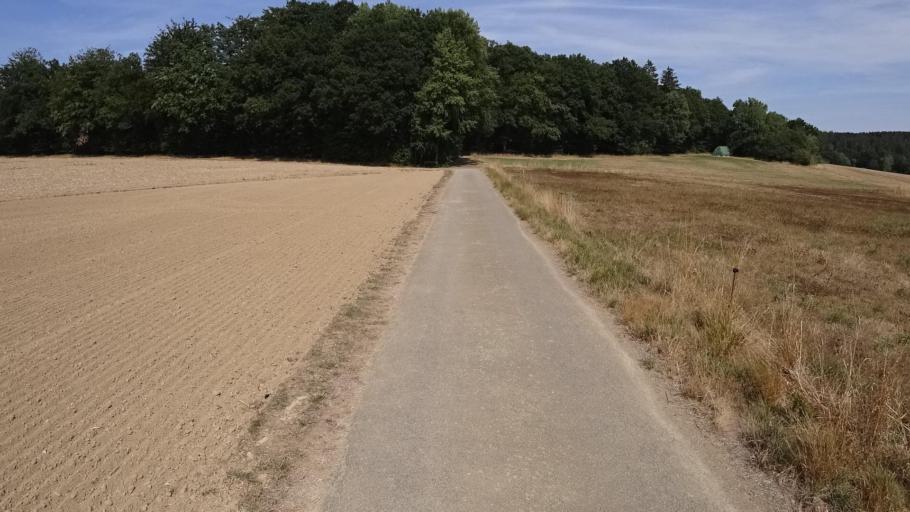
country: DE
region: Rheinland-Pfalz
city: Kisselbach
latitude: 50.0596
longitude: 7.6148
